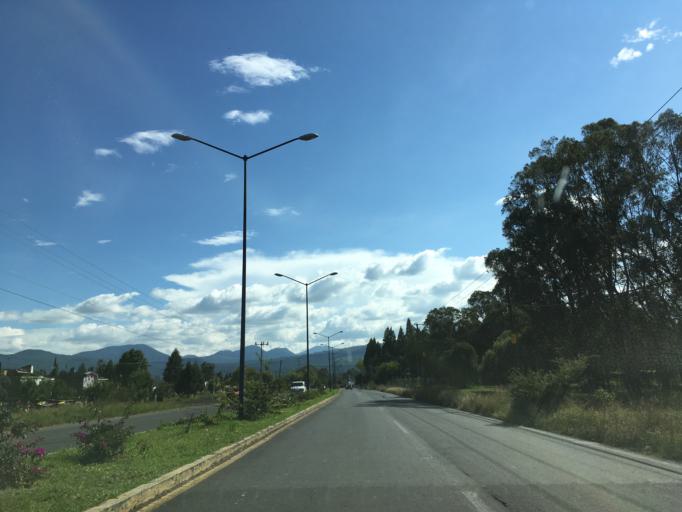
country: MX
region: Michoacan
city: Zacapu
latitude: 19.8260
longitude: -101.7752
